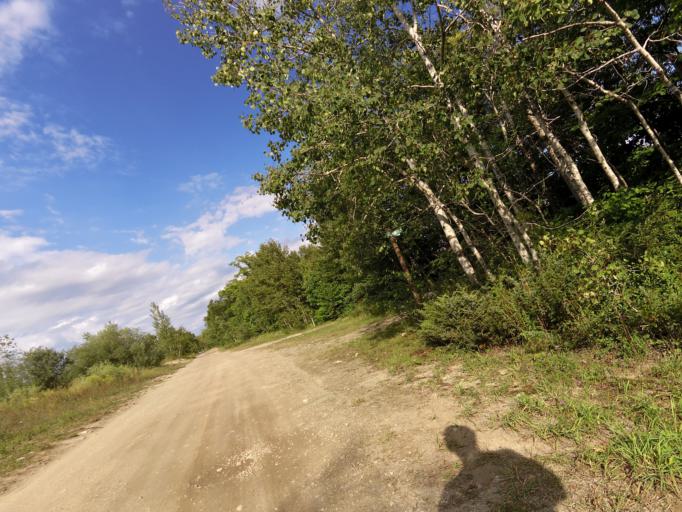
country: CA
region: Ontario
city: Tobermory
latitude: 45.2310
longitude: -81.6456
